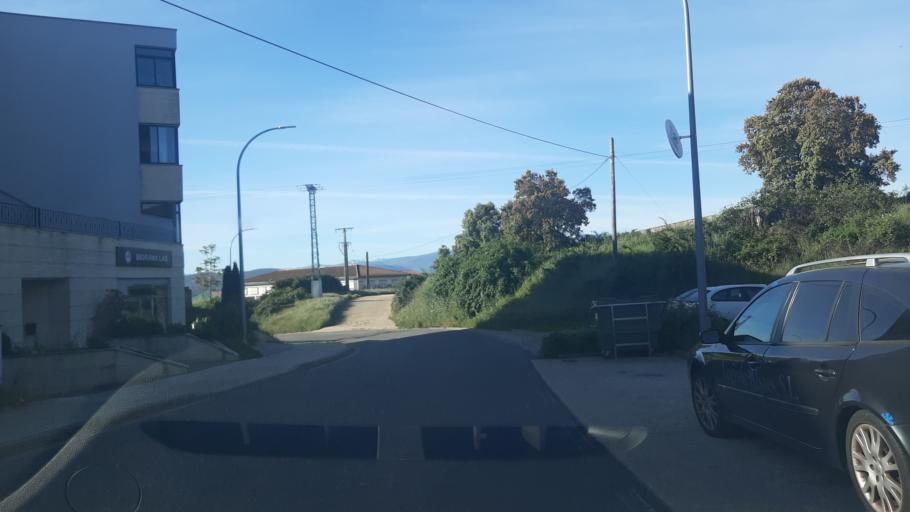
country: ES
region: Castille and Leon
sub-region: Provincia de Salamanca
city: Guijuelo
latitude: 40.5521
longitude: -5.6680
